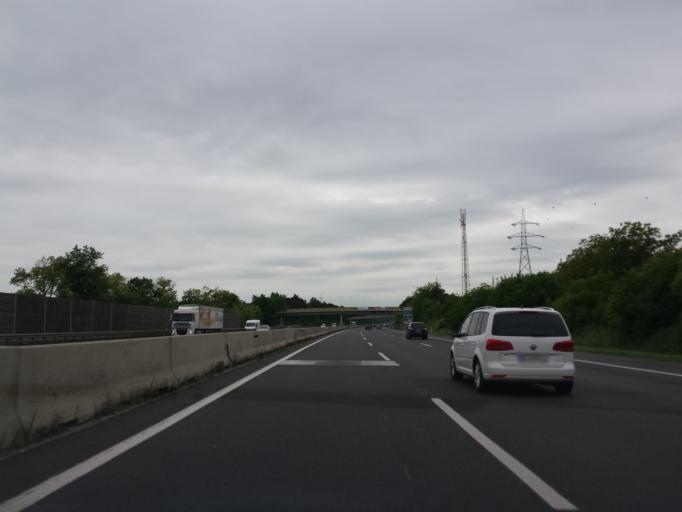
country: AT
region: Lower Austria
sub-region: Politischer Bezirk Wiener Neustadt
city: Felixdorf
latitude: 47.8773
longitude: 16.2014
